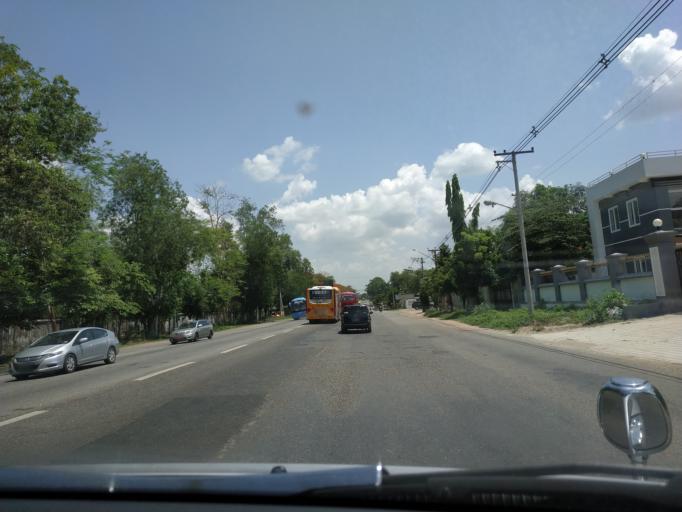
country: MM
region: Yangon
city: Yangon
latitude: 16.9953
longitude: 96.1307
